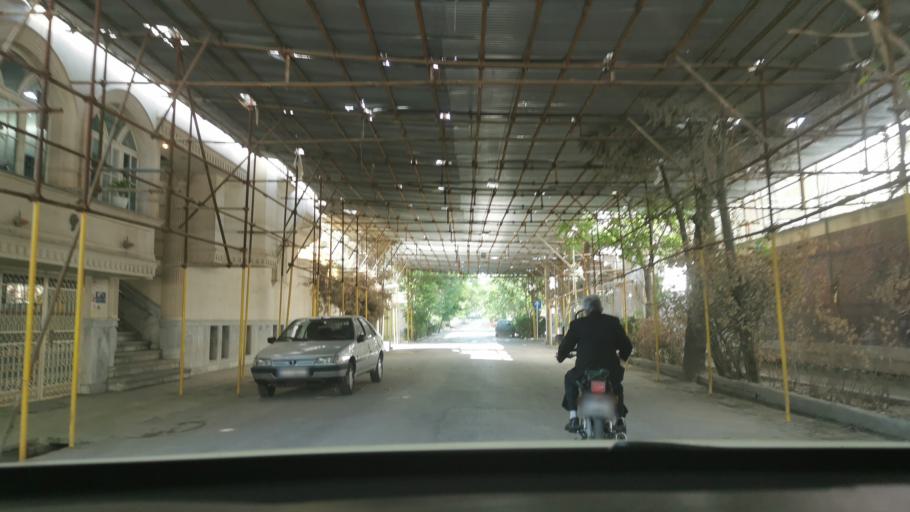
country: IR
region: Razavi Khorasan
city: Mashhad
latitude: 36.2869
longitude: 59.5760
